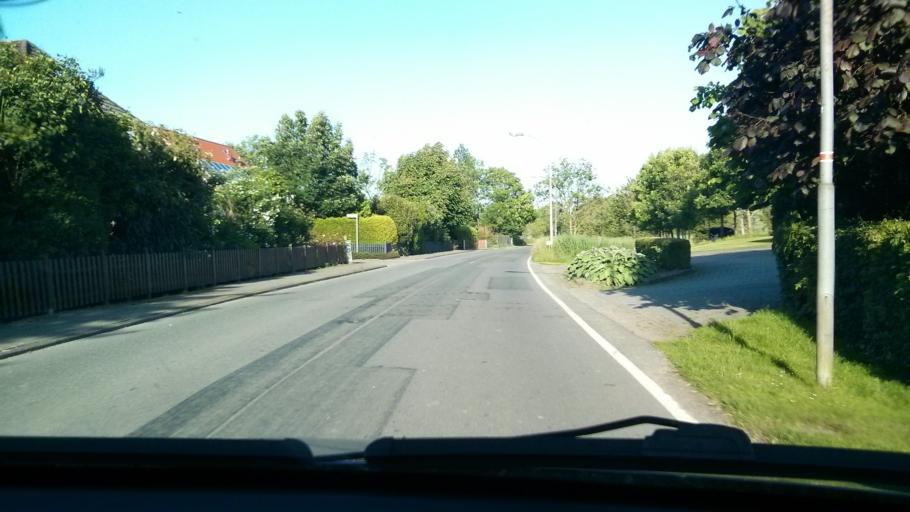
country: DE
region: Lower Saxony
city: Nordenham
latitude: 53.4442
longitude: 8.5032
